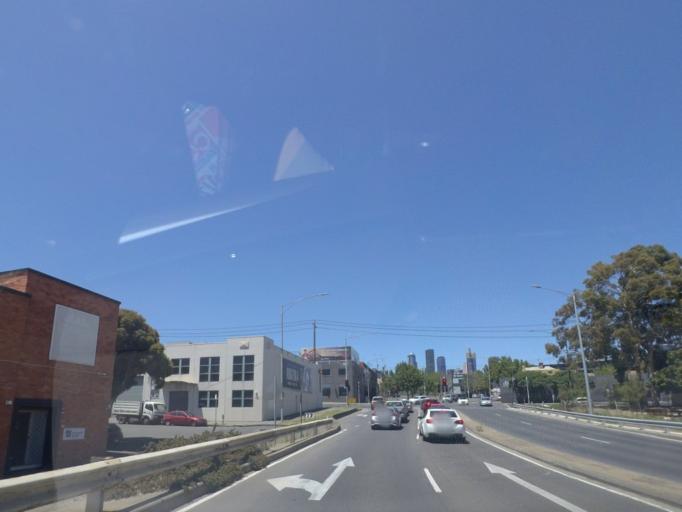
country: AU
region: Victoria
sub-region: Melbourne
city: North Melbourne
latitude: -37.8053
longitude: 144.9421
